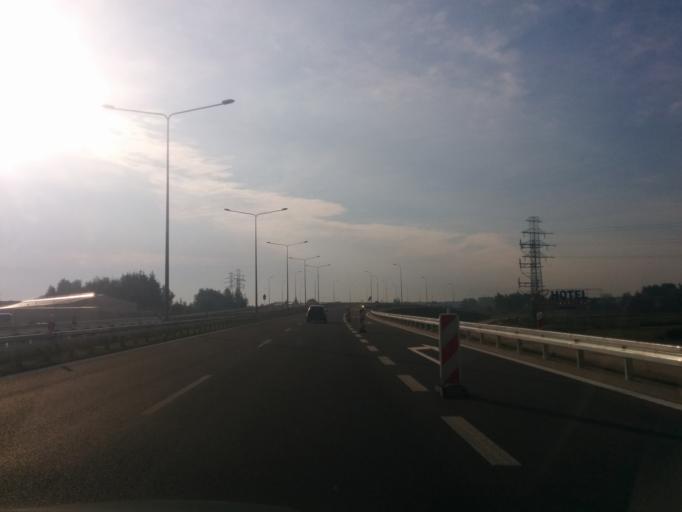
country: PL
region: Masovian Voivodeship
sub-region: Powiat pruszkowski
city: Nowe Grocholice
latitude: 52.1174
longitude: 20.8862
